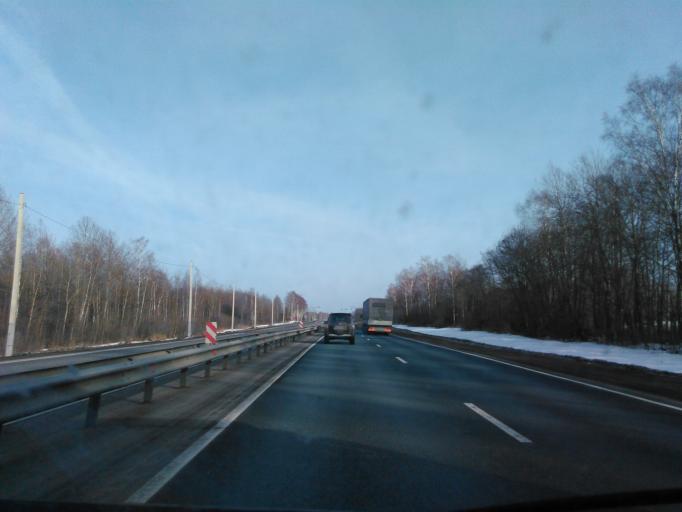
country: RU
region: Smolensk
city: Verkhnedneprovskiy
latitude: 55.1819
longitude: 33.5570
